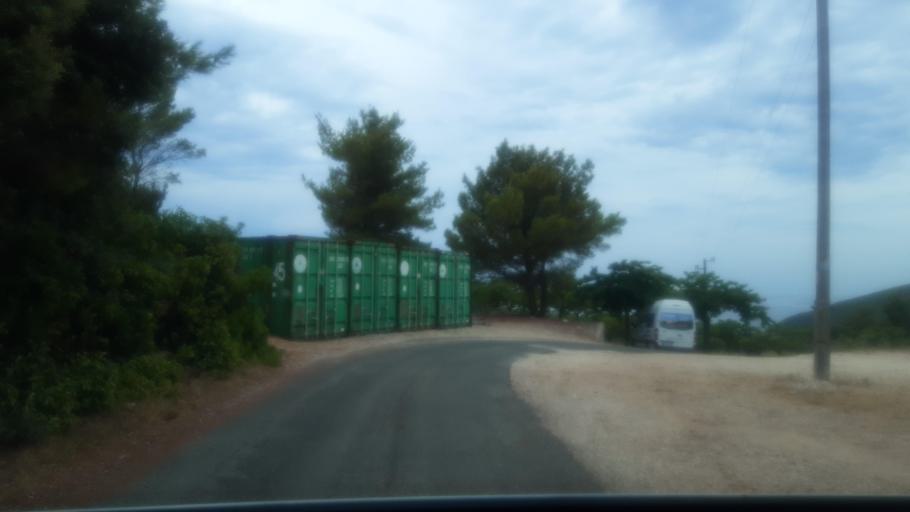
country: HR
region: Dubrovacko-Neretvanska
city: Blato
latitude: 42.7555
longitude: 17.4688
